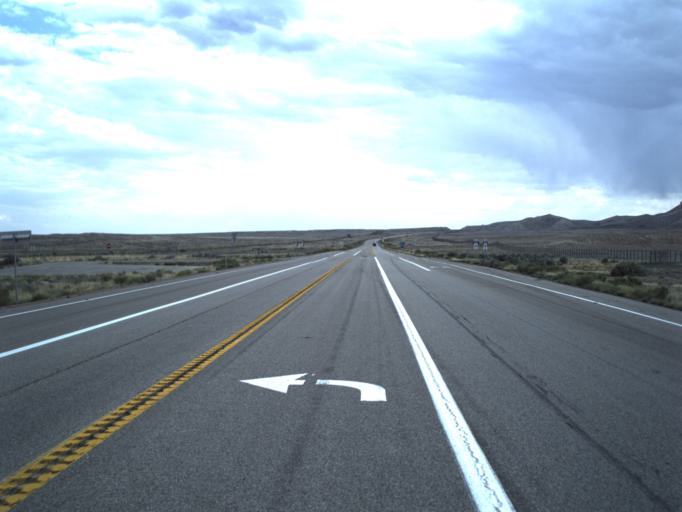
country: US
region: Utah
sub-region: Emery County
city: Huntington
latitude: 39.4344
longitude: -110.8673
